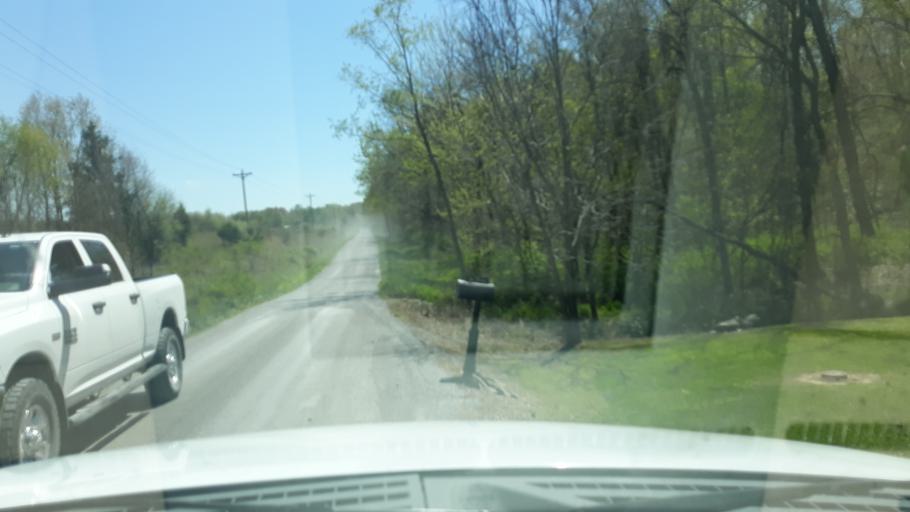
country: US
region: Illinois
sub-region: Saline County
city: Harrisburg
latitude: 37.8743
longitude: -88.6422
